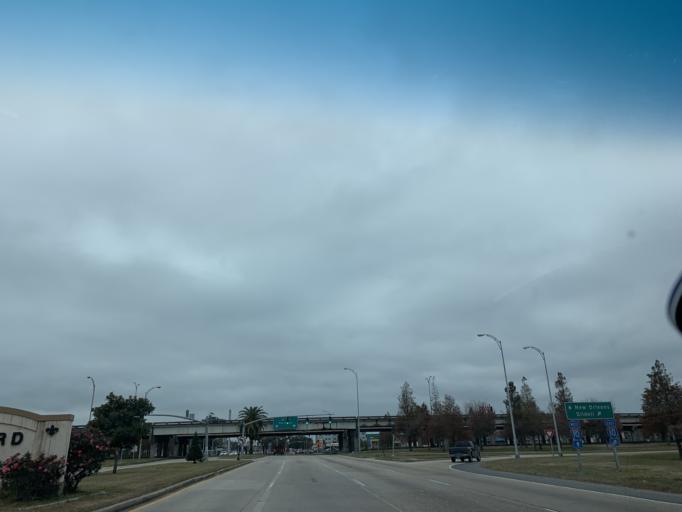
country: US
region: Louisiana
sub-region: Saint Bernard Parish
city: Arabi
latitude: 30.0452
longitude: -89.9602
